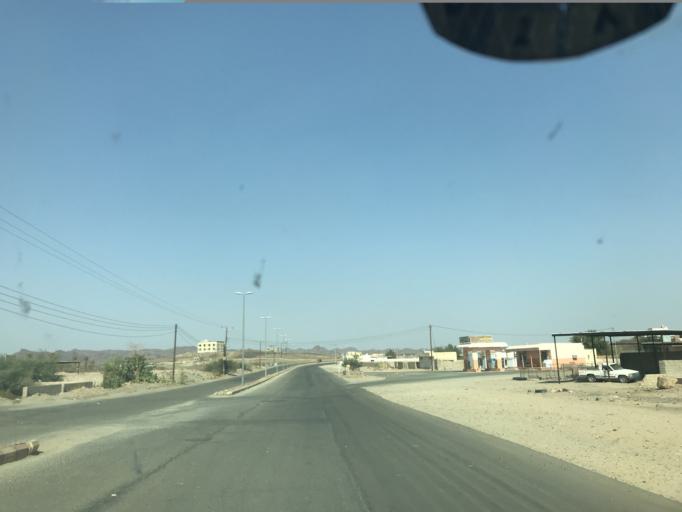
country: SA
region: Mintaqat al Bahah
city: Al Bahah
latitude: 20.4389
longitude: 41.9207
